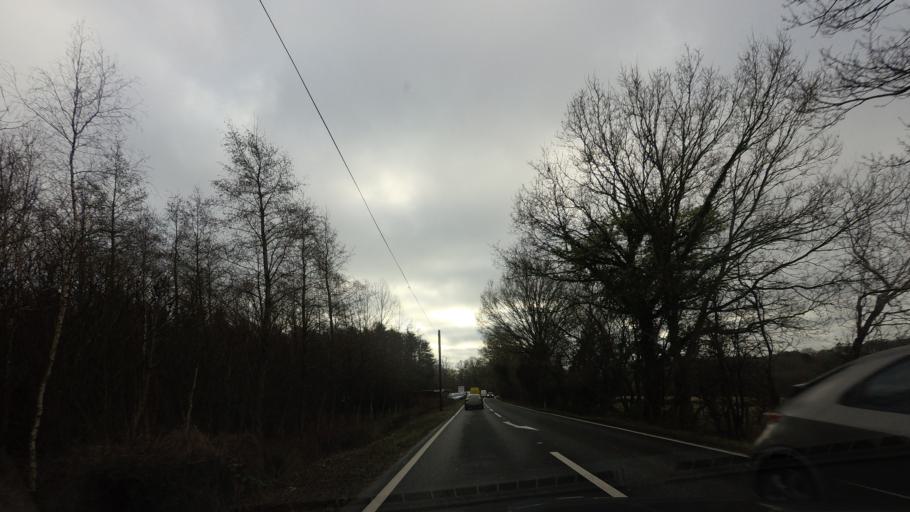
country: GB
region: England
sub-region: East Sussex
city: Wadhurst
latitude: 51.0798
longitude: 0.4182
